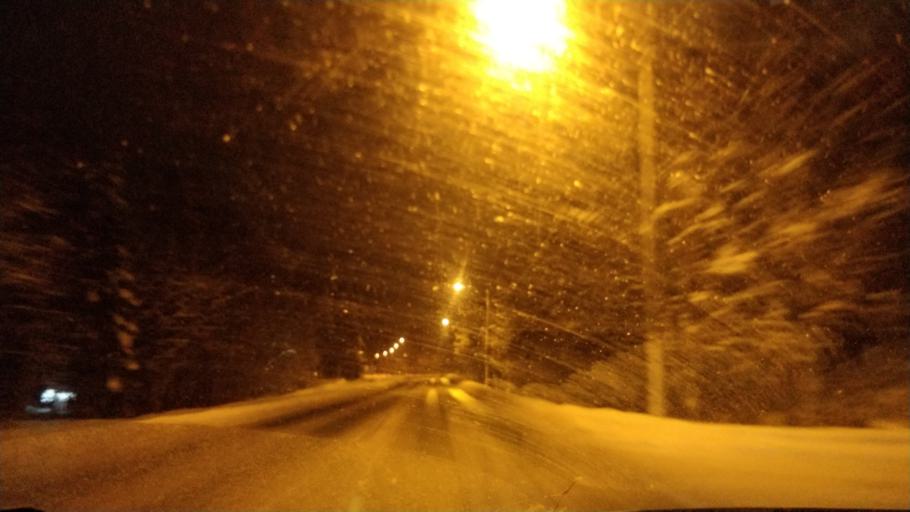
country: FI
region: Lapland
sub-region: Rovaniemi
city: Rovaniemi
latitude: 66.3814
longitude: 25.3789
